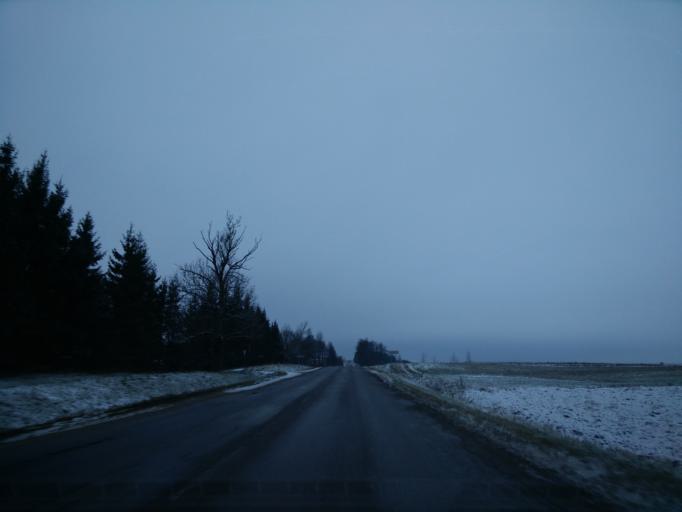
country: LT
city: Kelme
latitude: 55.6139
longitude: 22.9037
